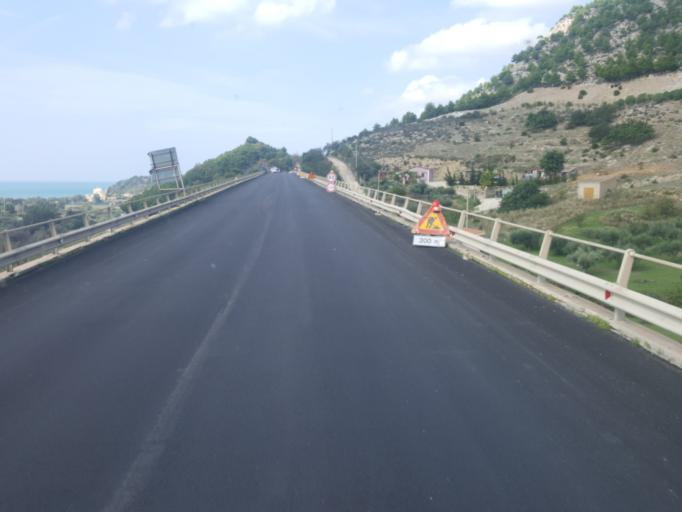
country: IT
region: Sicily
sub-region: Agrigento
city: Siculiana
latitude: 37.3372
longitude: 13.4098
